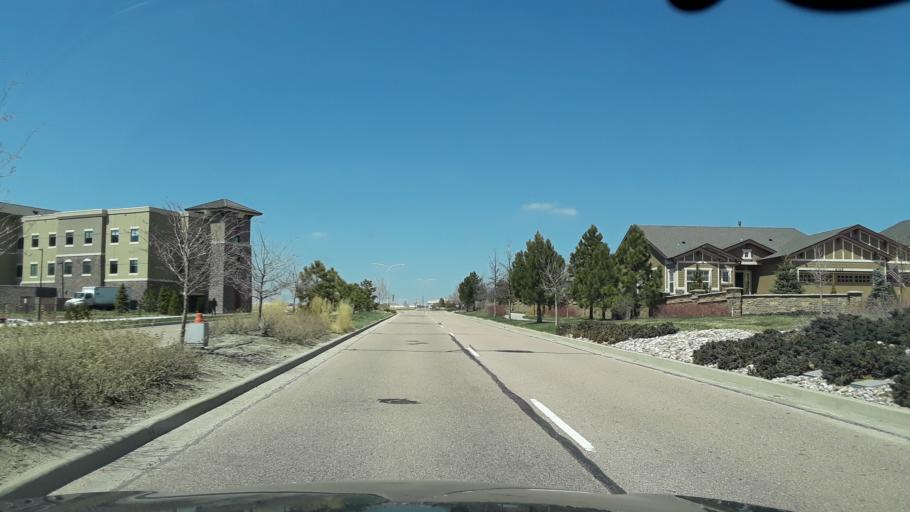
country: US
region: Colorado
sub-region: El Paso County
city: Black Forest
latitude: 38.9635
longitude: -104.7328
